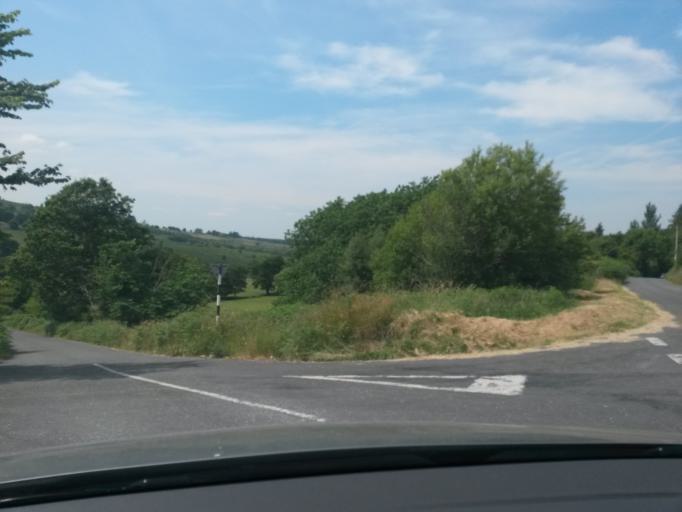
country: IE
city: Jobstown
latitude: 53.1744
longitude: -6.4158
